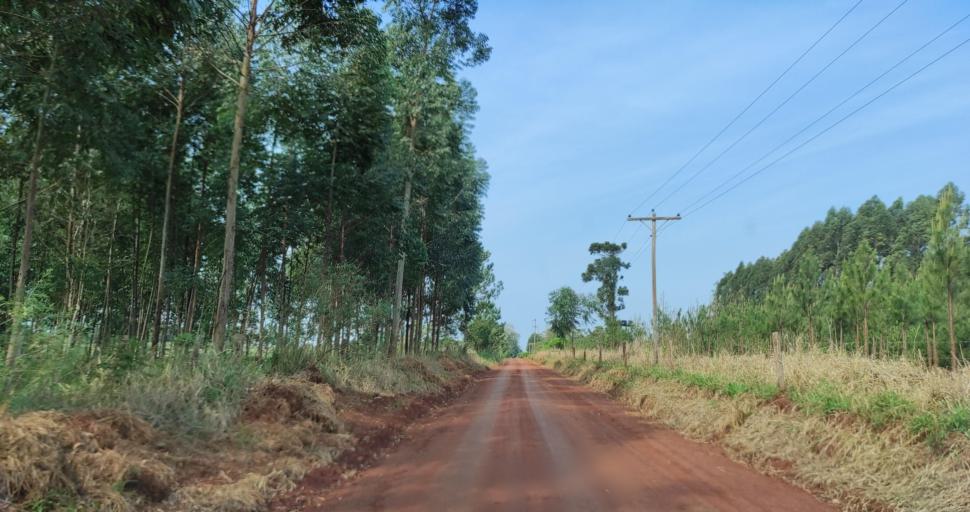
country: AR
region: Misiones
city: Garuhape
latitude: -26.8663
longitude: -55.0037
